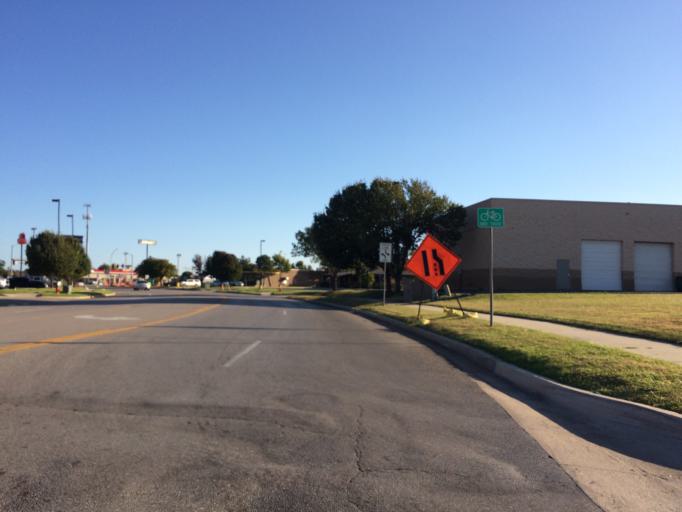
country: US
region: Oklahoma
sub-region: Cleveland County
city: Norman
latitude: 35.2314
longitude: -97.4900
